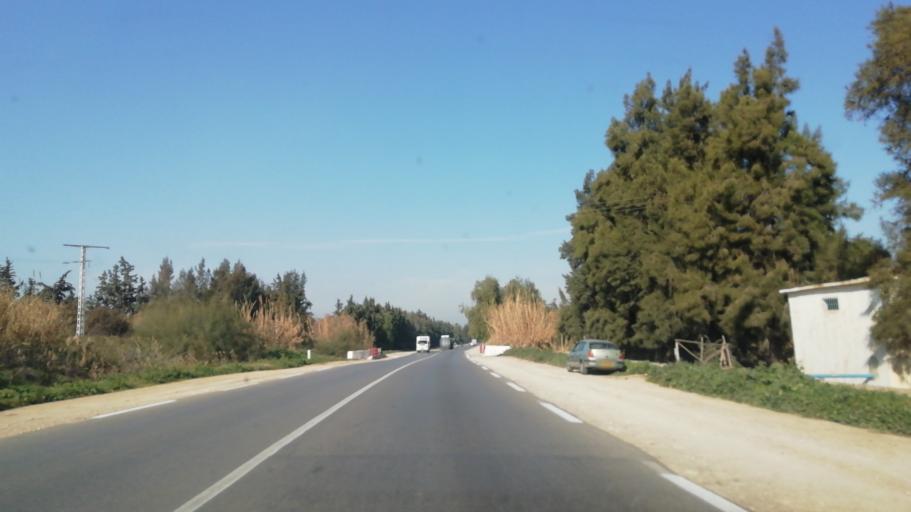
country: DZ
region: Relizane
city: Relizane
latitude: 35.7249
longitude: 0.4813
